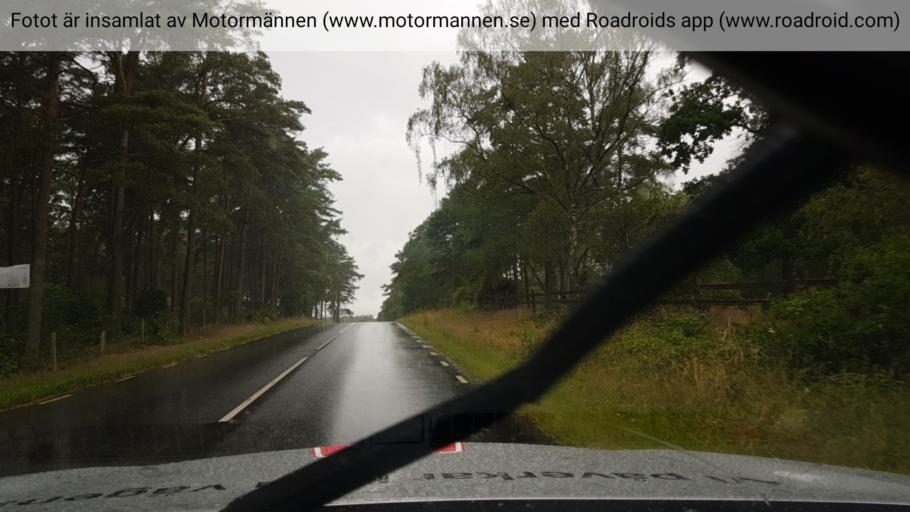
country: SE
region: Blekinge
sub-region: Solvesborgs Kommun
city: Soelvesborg
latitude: 56.0150
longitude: 14.6877
